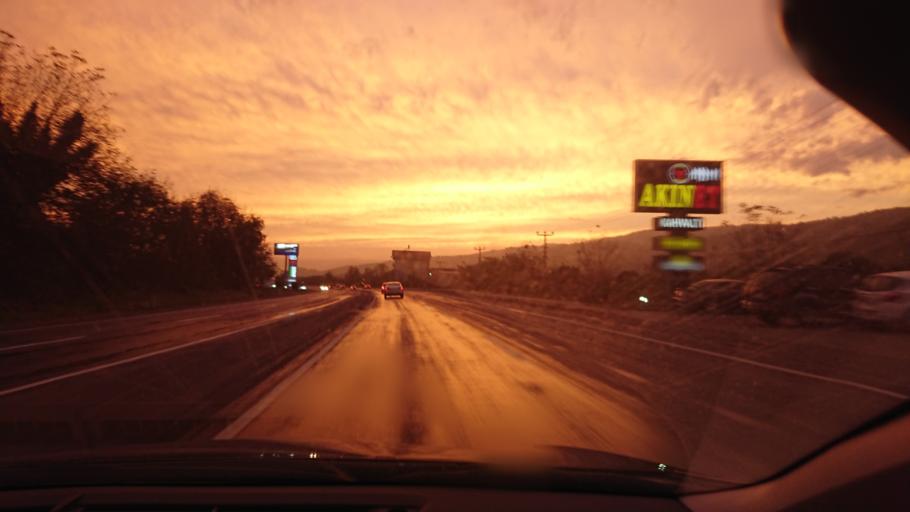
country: TR
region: Zonguldak
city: Gokcebey
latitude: 41.2728
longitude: 32.0541
